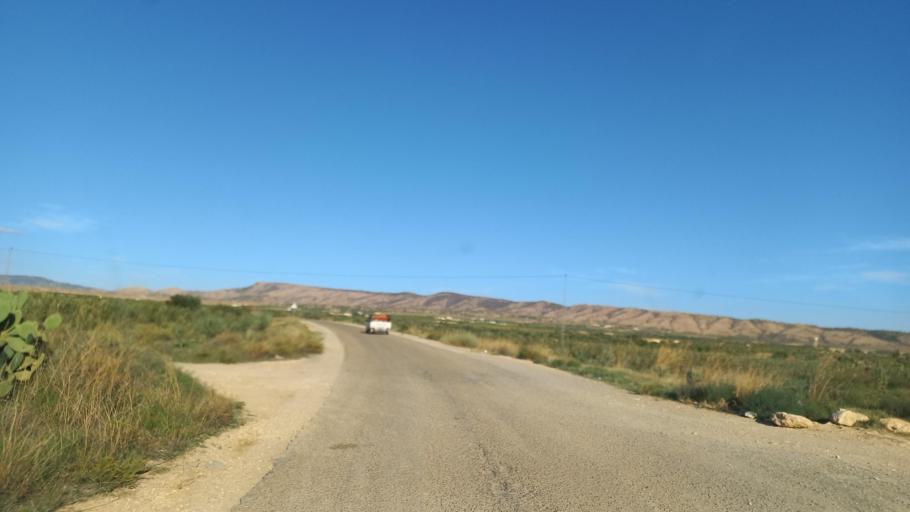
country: TN
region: Al Qasrayn
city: Sbiba
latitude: 35.3338
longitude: 9.0952
